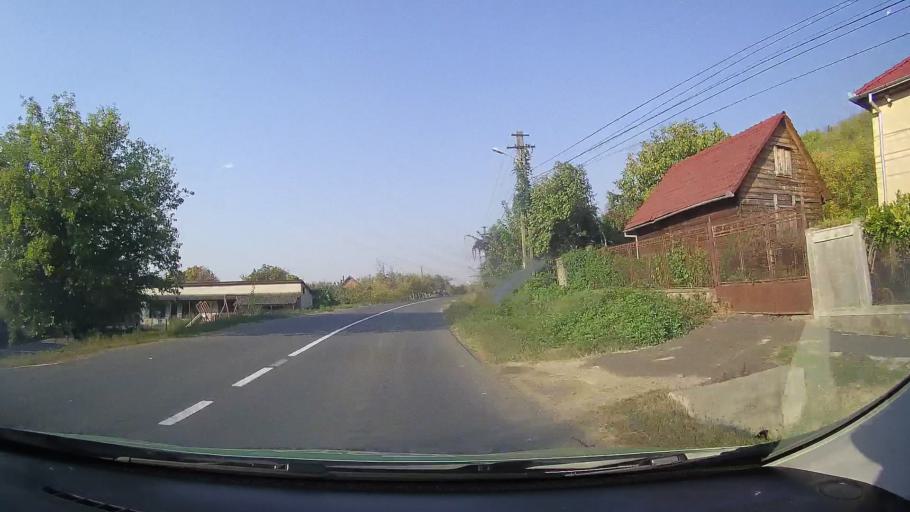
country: RO
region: Arad
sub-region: Comuna Paulis
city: Paulis
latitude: 46.1151
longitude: 21.5962
